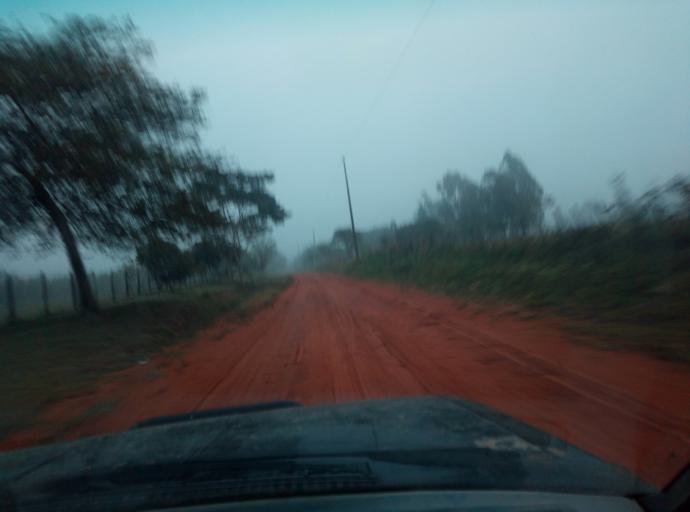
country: PY
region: Caaguazu
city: Doctor Cecilio Baez
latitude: -25.1550
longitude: -56.2876
